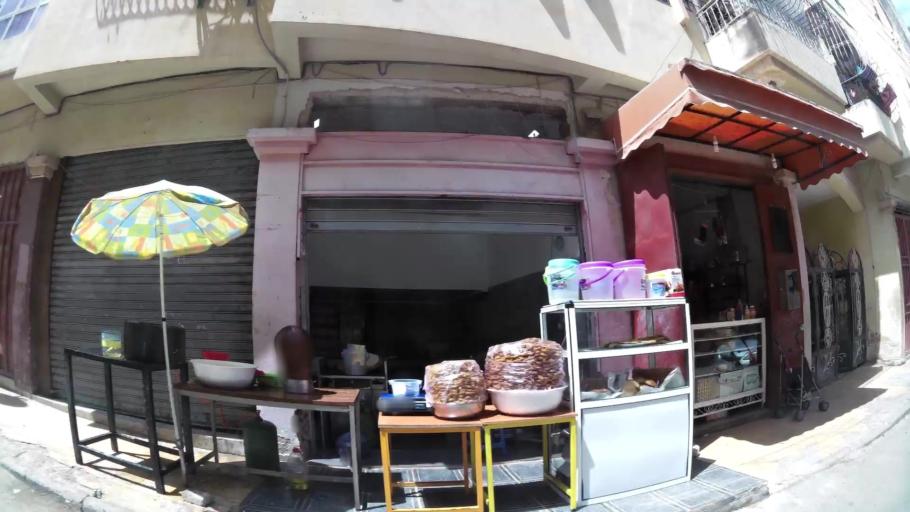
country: MA
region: Fes-Boulemane
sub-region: Fes
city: Fes
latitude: 34.0101
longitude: -4.9876
